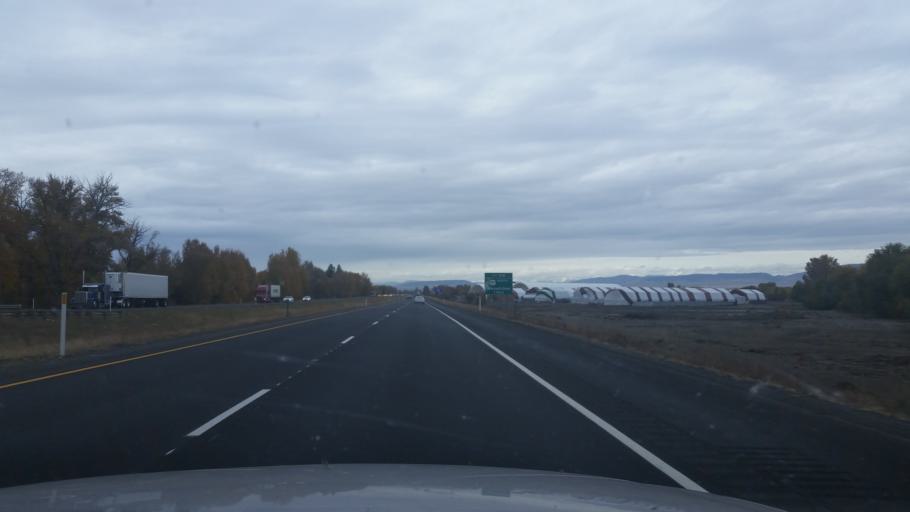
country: US
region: Washington
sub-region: Kittitas County
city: Ellensburg
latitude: 46.9910
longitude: -120.5724
